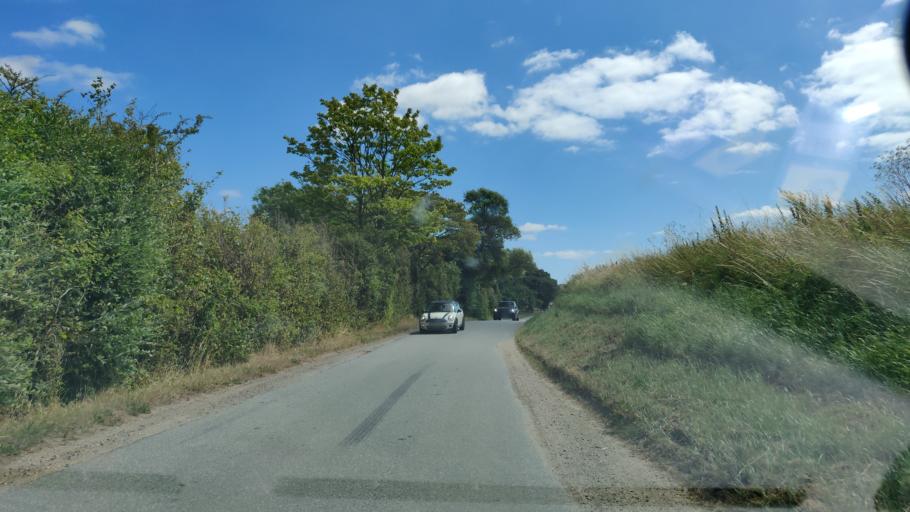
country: DK
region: South Denmark
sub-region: Fredericia Kommune
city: Taulov
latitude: 55.5242
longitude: 9.5456
